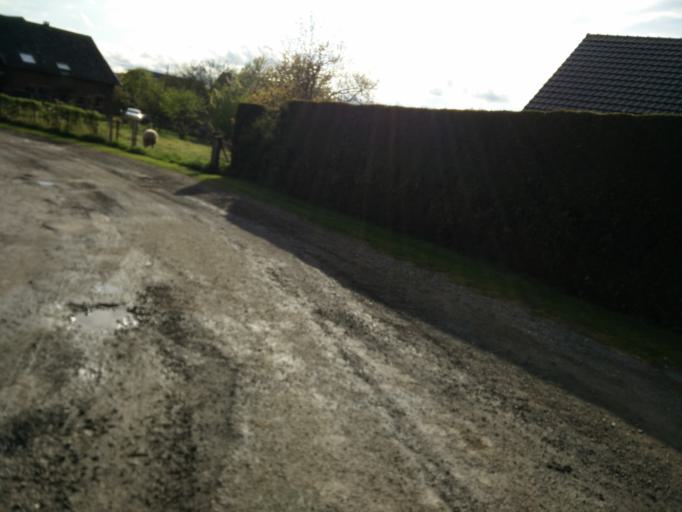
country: BE
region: Wallonia
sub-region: Province de Liege
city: Dalhem
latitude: 50.7265
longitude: 5.7739
